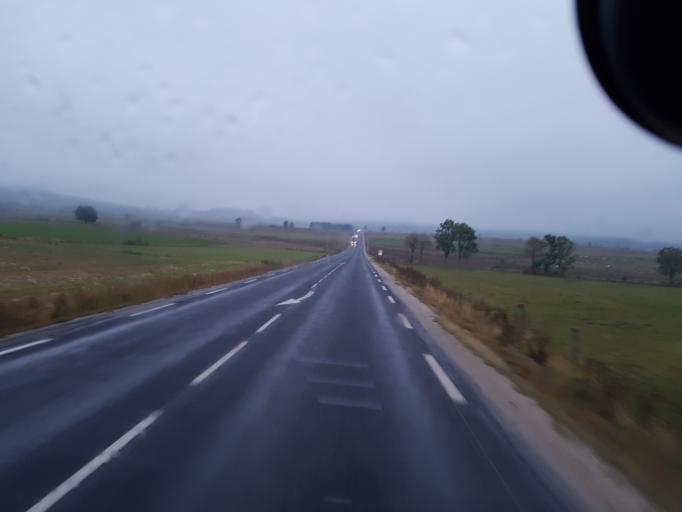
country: FR
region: Languedoc-Roussillon
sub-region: Departement de la Lozere
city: Langogne
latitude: 44.8168
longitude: 3.8741
